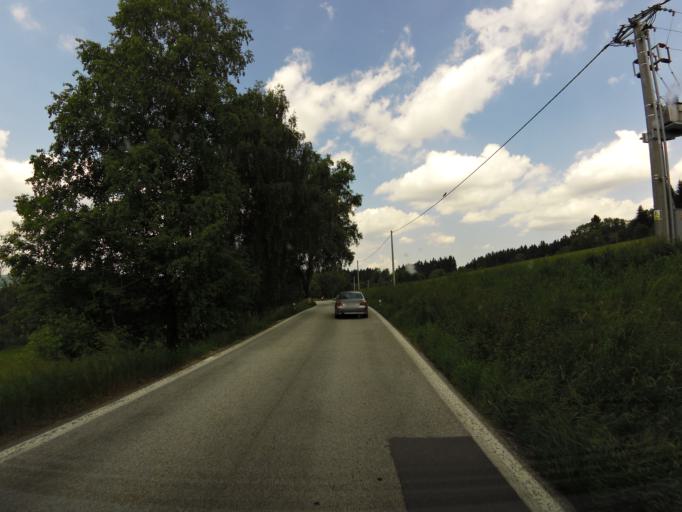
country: CZ
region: Jihocesky
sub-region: Okres Cesky Krumlov
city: Horni Plana
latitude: 48.8000
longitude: 13.9754
